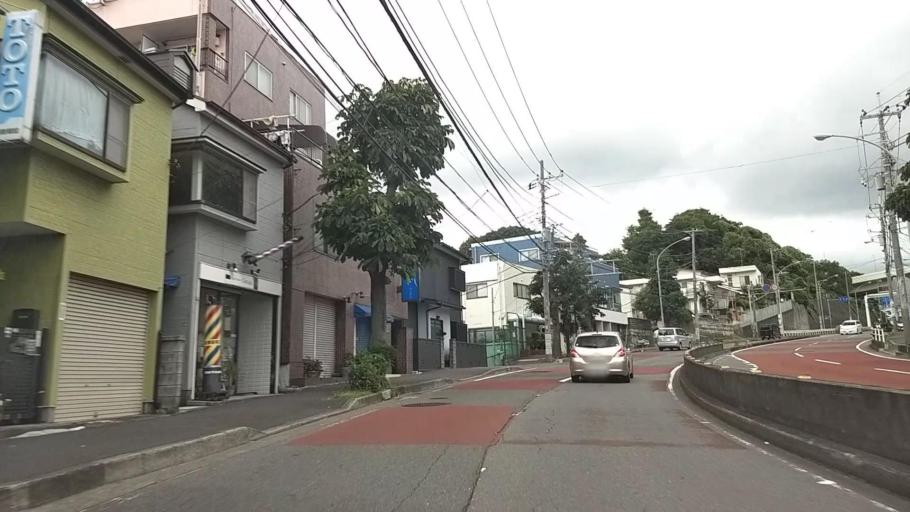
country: JP
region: Kanagawa
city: Yokohama
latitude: 35.4382
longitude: 139.5962
